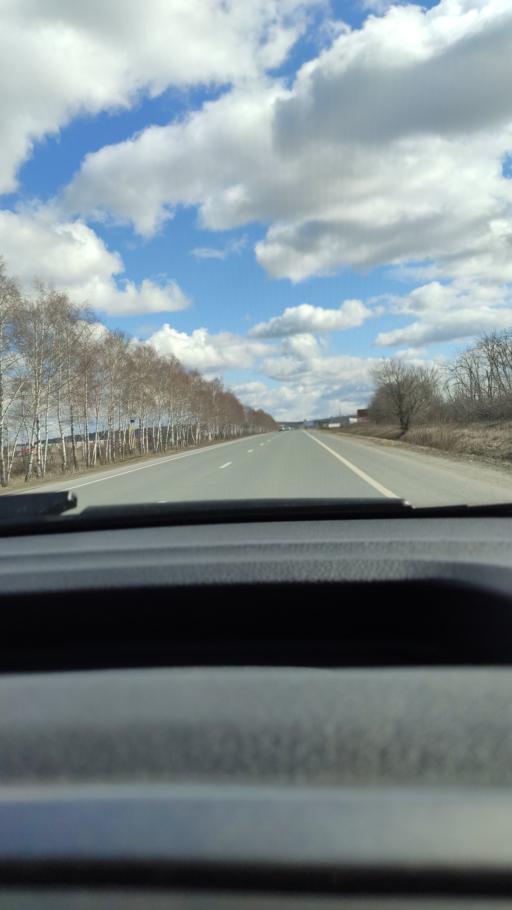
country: RU
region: Samara
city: Kurumoch
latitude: 53.4871
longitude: 50.0067
